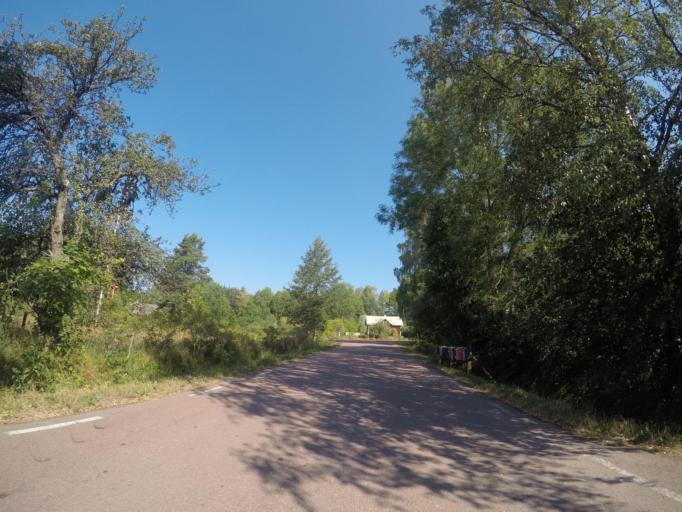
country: AX
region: Alands landsbygd
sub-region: Jomala
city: Jomala
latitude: 60.2109
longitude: 19.9733
